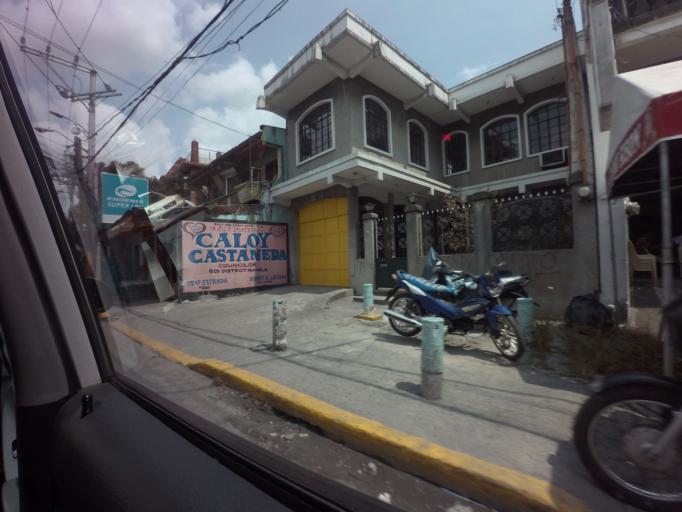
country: PH
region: Metro Manila
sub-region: San Juan
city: San Juan
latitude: 14.5908
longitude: 121.0101
